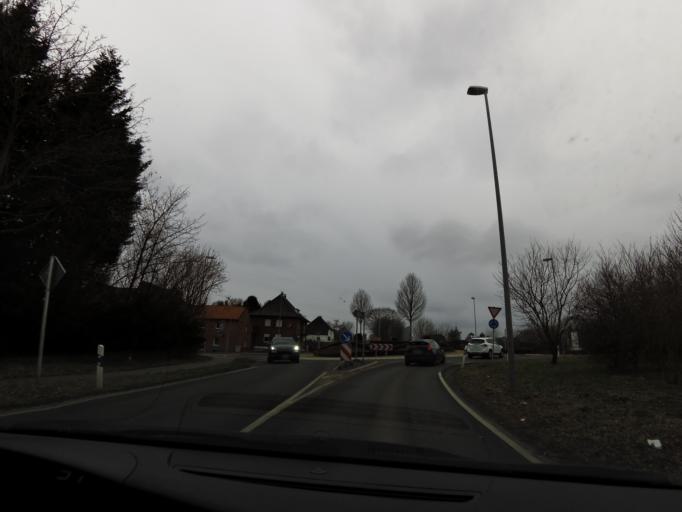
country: DE
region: North Rhine-Westphalia
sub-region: Regierungsbezirk Koln
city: Gangelt
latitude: 50.9917
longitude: 6.0054
